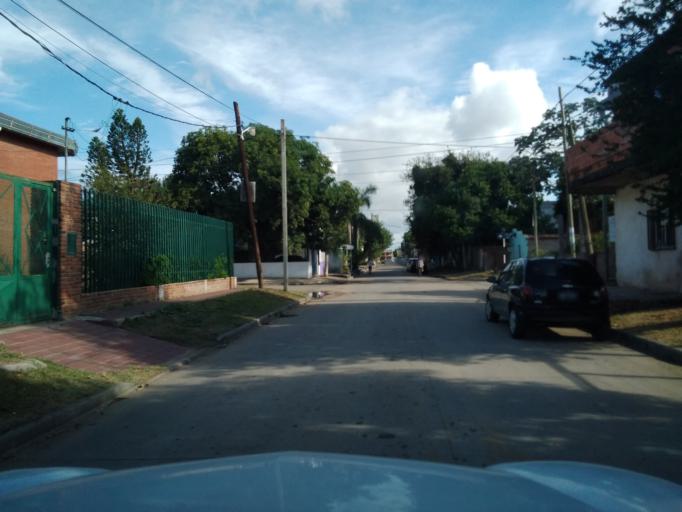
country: AR
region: Corrientes
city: Corrientes
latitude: -27.4648
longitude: -58.8125
